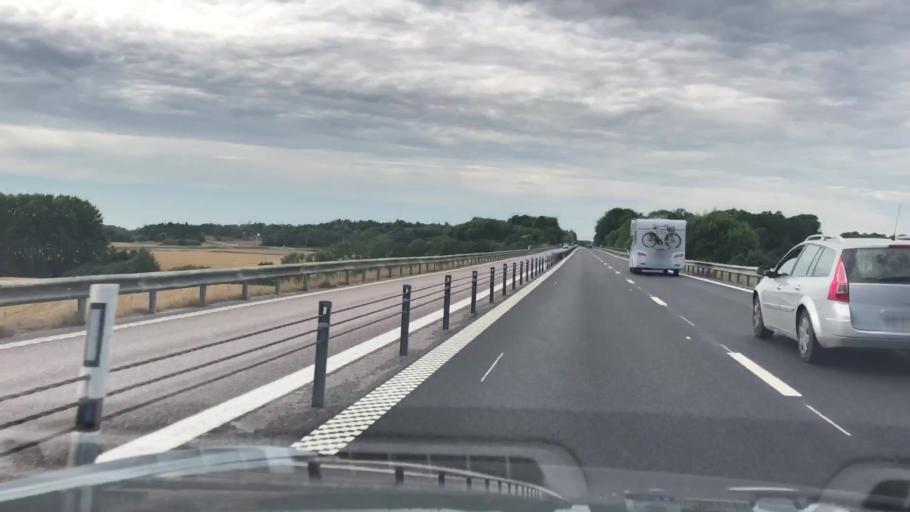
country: SE
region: Blekinge
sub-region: Ronneby Kommun
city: Brakne-Hoby
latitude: 56.2165
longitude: 15.1112
